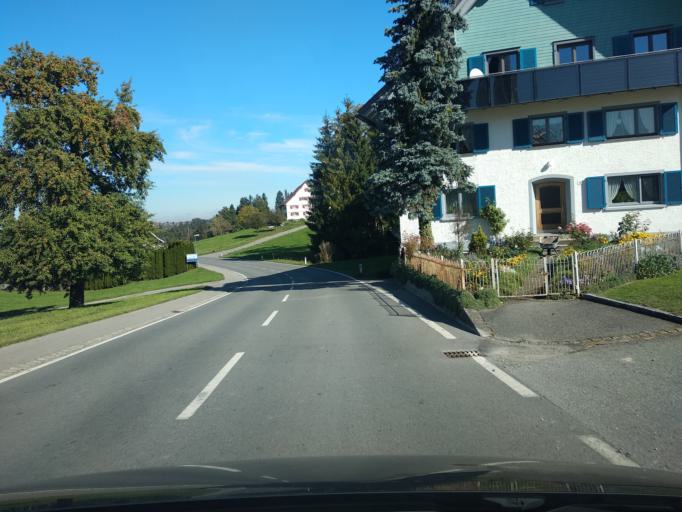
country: AT
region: Vorarlberg
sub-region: Politischer Bezirk Bregenz
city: Hohenweiler
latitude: 47.5889
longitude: 9.7815
